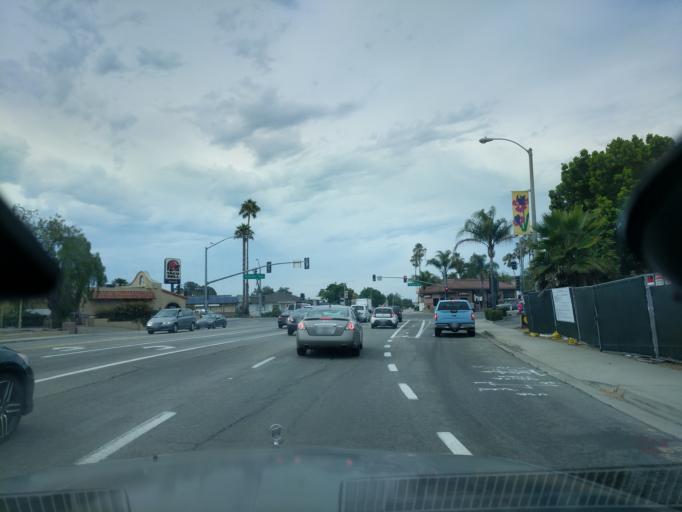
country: US
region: California
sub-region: Santa Barbara County
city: Goleta
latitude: 34.4368
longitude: -119.8308
